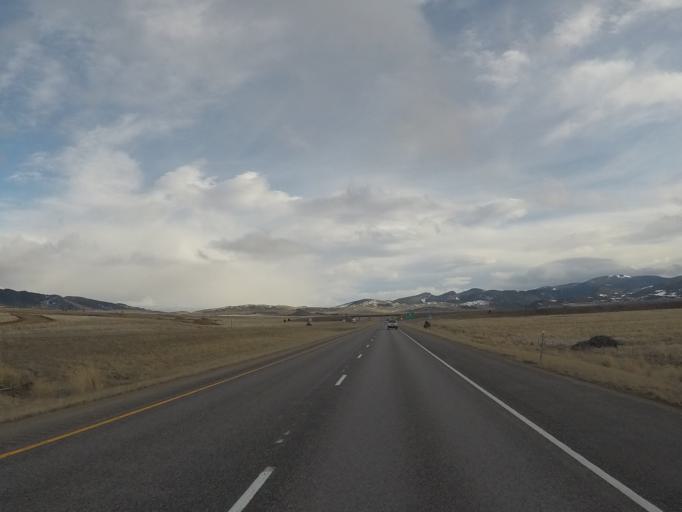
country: US
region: Montana
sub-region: Deer Lodge County
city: Warm Springs
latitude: 46.1027
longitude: -112.7953
